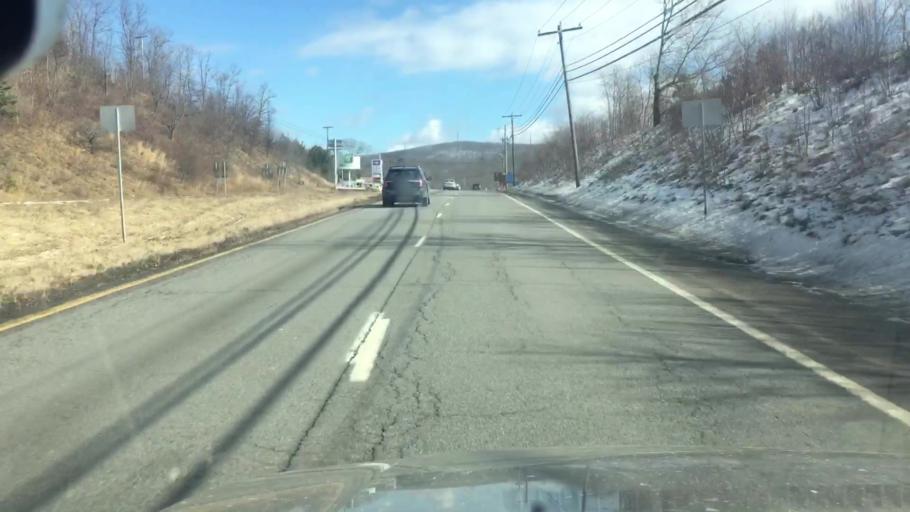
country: US
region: Pennsylvania
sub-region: Luzerne County
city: Hudson
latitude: 41.2497
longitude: -75.8152
